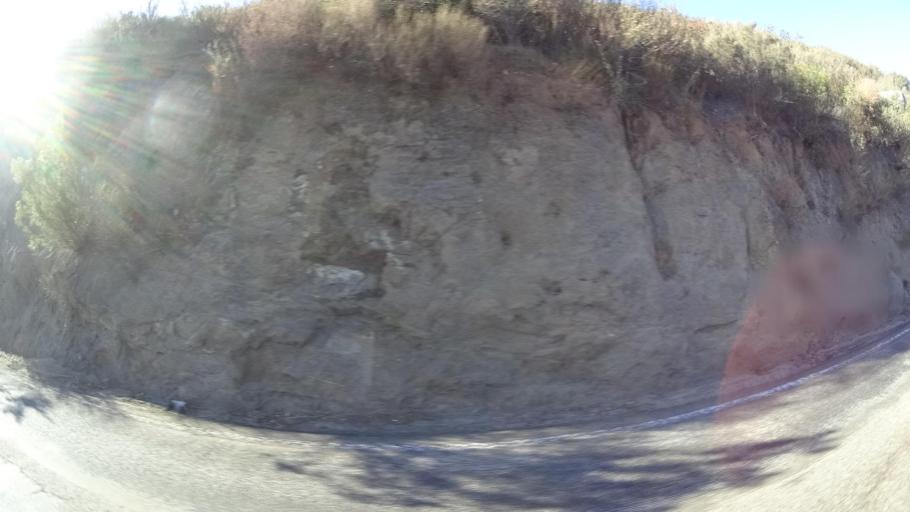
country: MX
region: Baja California
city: Tecate
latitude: 32.5944
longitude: -116.6674
